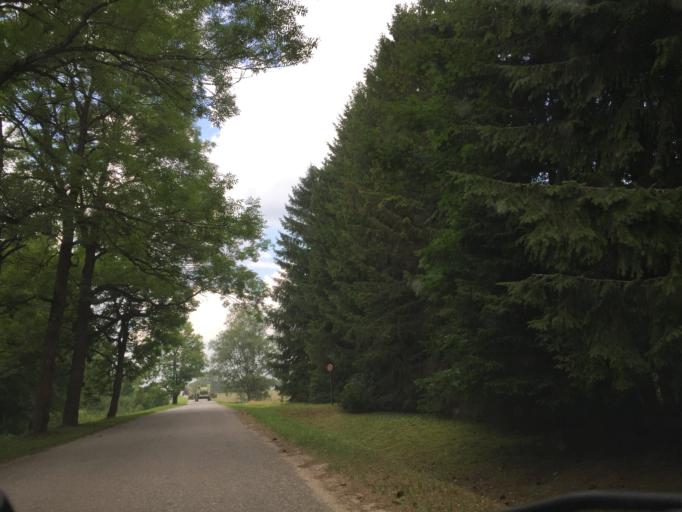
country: LT
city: Naujoji Akmene
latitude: 56.3452
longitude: 23.0605
